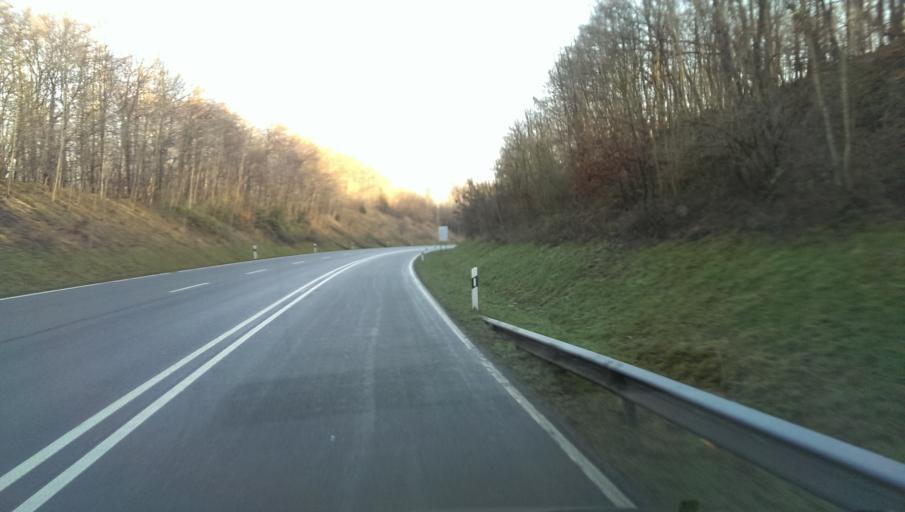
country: DE
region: North Rhine-Westphalia
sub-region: Regierungsbezirk Detmold
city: Bad Driburg
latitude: 51.7402
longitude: 8.9898
